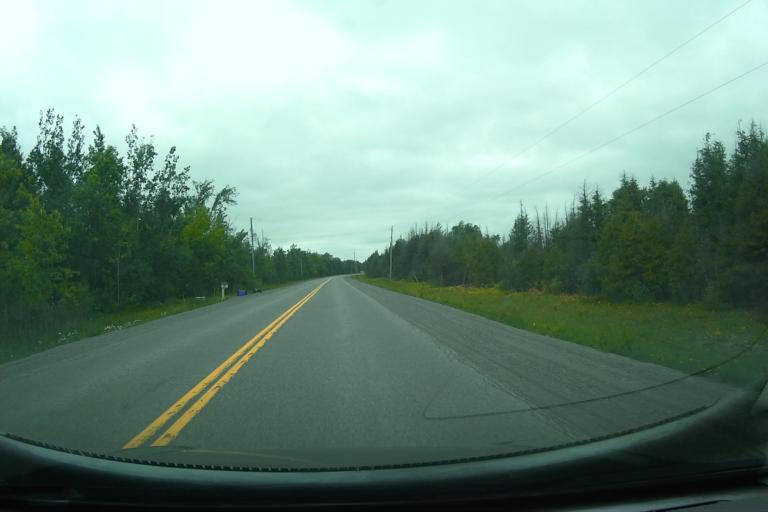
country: CA
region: Ontario
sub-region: Lanark County
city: Smiths Falls
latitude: 45.0274
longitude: -75.8586
